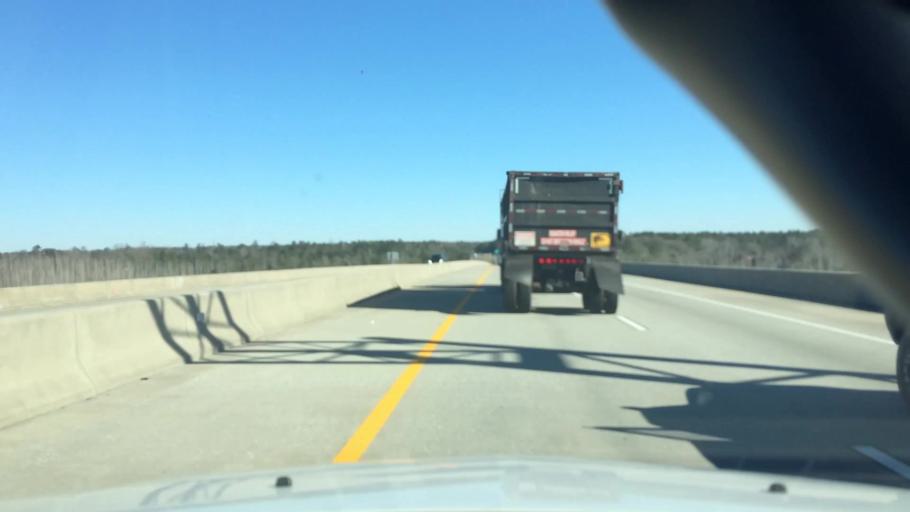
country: US
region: North Carolina
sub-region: New Hanover County
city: Wrightsboro
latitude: 34.3011
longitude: -77.9575
